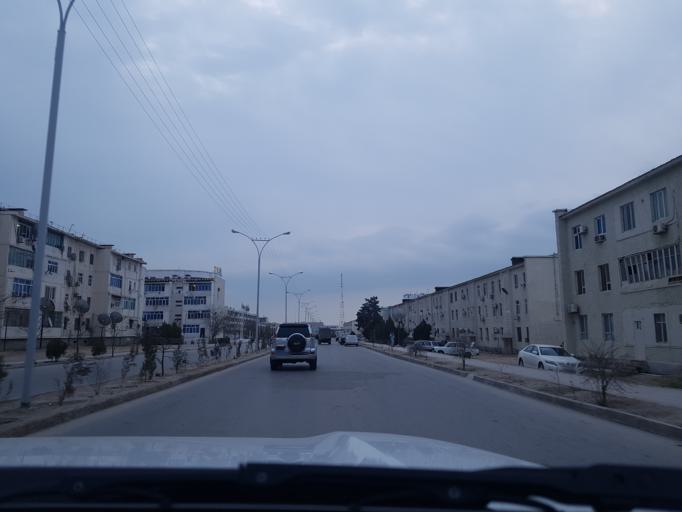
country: TM
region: Balkan
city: Balkanabat
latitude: 39.5239
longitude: 54.3517
